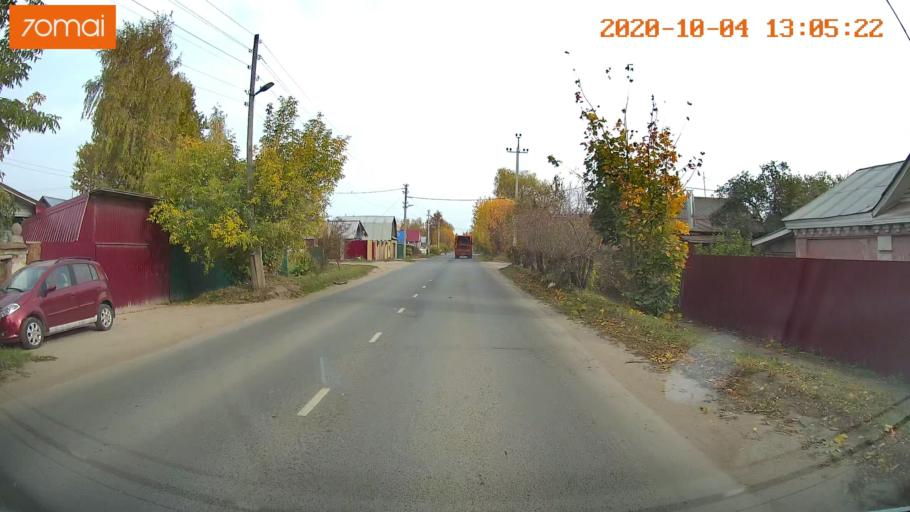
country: RU
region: Ivanovo
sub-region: Gorod Ivanovo
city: Ivanovo
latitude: 57.0421
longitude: 40.9542
